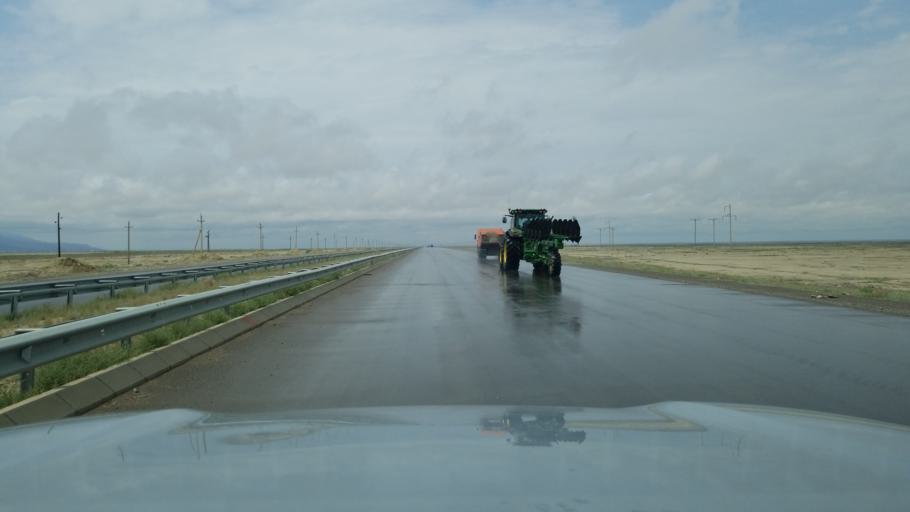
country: TM
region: Balkan
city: Gazanjyk
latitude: 39.1795
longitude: 55.8058
